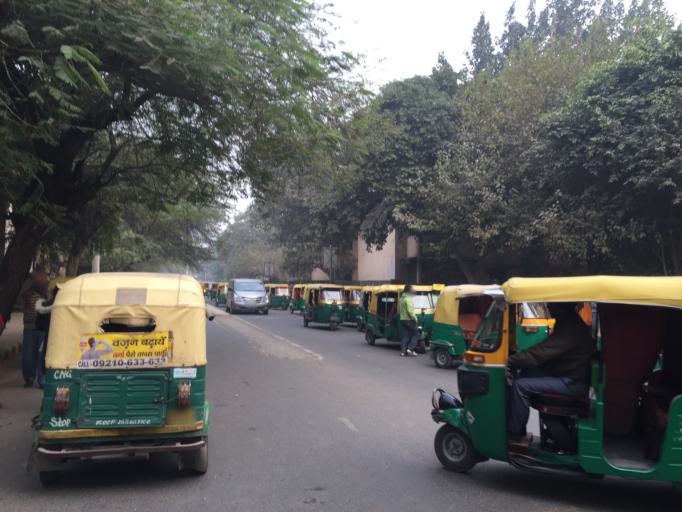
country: IN
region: NCT
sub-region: New Delhi
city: New Delhi
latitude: 28.5783
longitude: 77.1972
